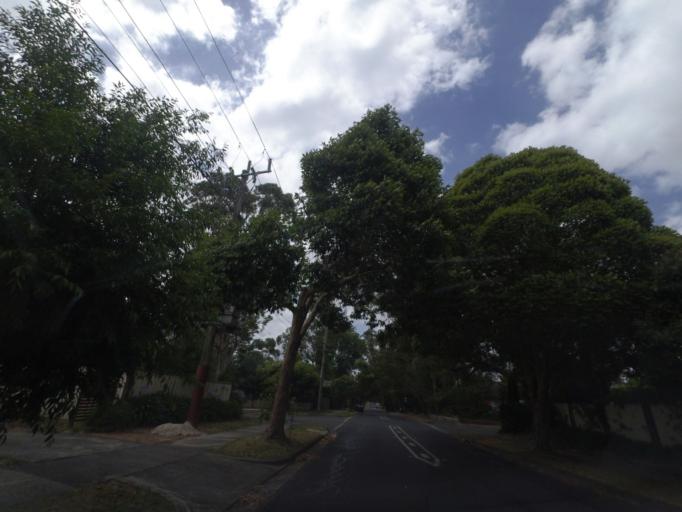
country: AU
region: Victoria
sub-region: Maroondah
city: Croydon South
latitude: -37.8086
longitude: 145.2826
